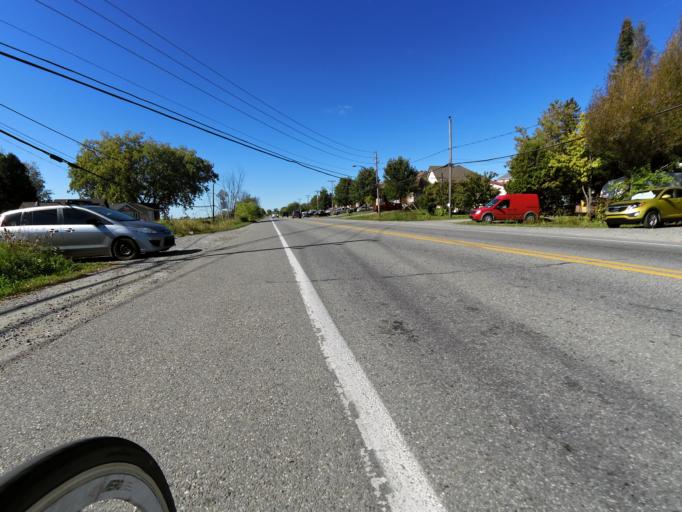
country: CA
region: Quebec
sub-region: Outaouais
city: Gatineau
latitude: 45.5213
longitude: -75.4981
